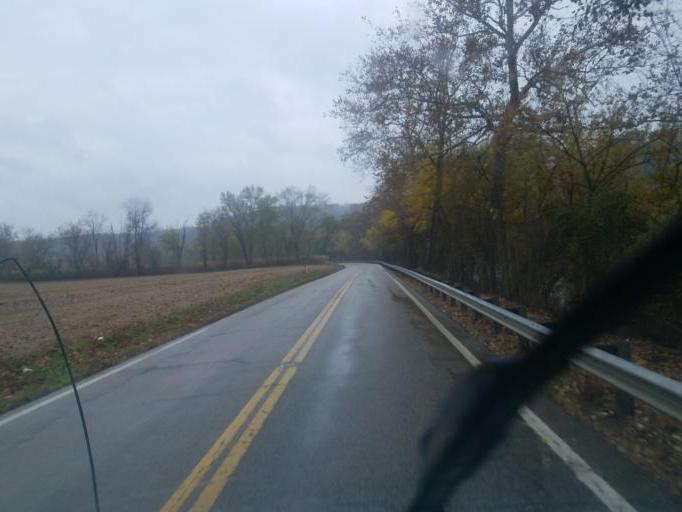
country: US
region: Ohio
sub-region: Morgan County
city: McConnelsville
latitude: 39.5980
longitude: -81.8119
